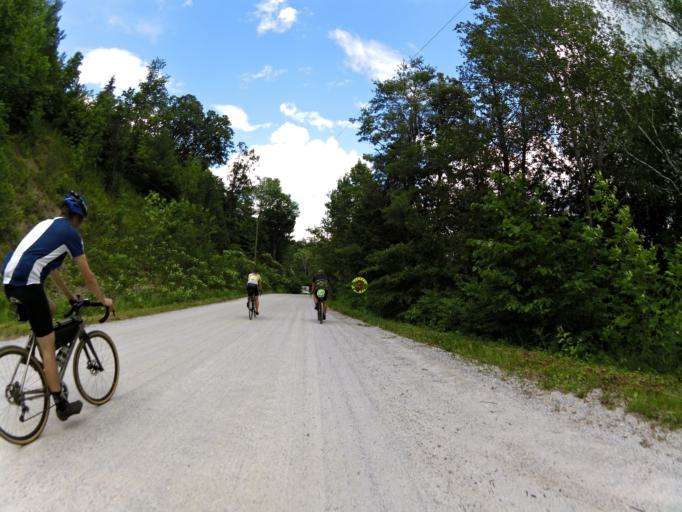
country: CA
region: Ontario
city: Renfrew
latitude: 45.1343
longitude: -76.6319
